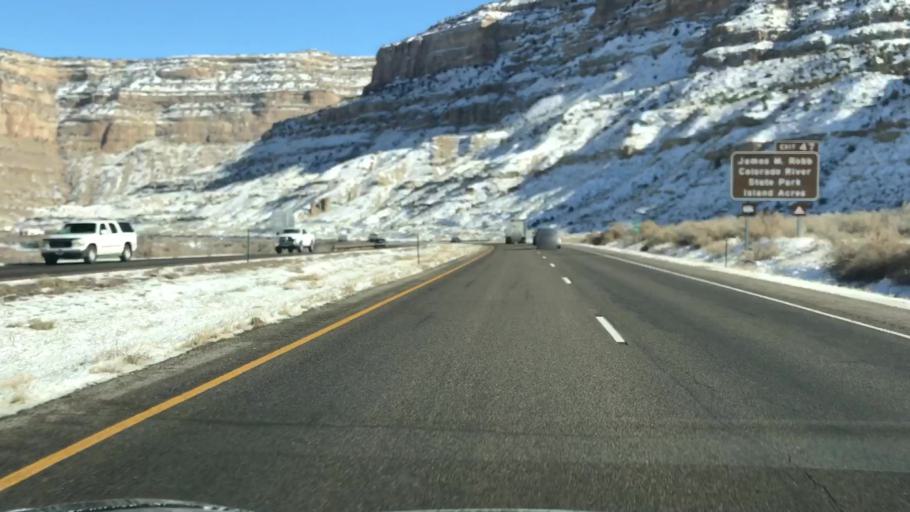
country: US
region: Colorado
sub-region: Mesa County
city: Palisade
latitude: 39.1503
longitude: -108.3071
